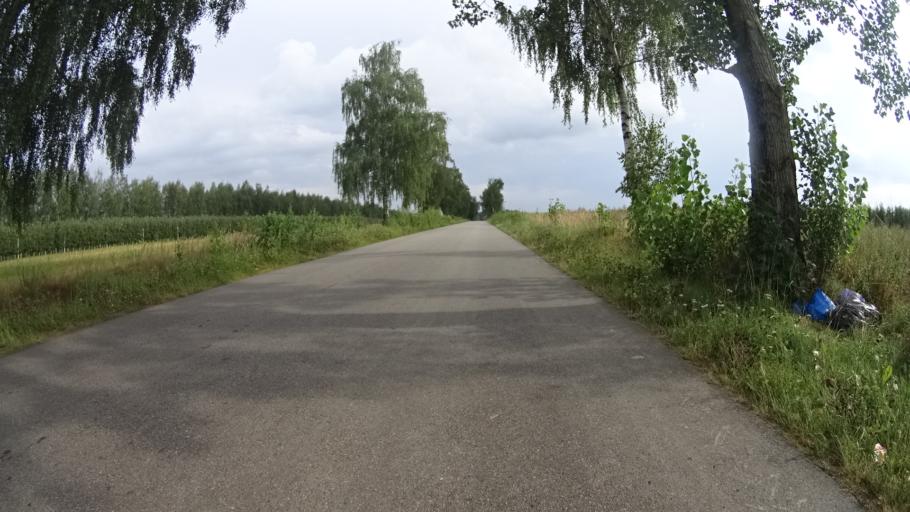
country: PL
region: Masovian Voivodeship
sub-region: Powiat grojecki
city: Goszczyn
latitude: 51.6958
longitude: 20.8564
